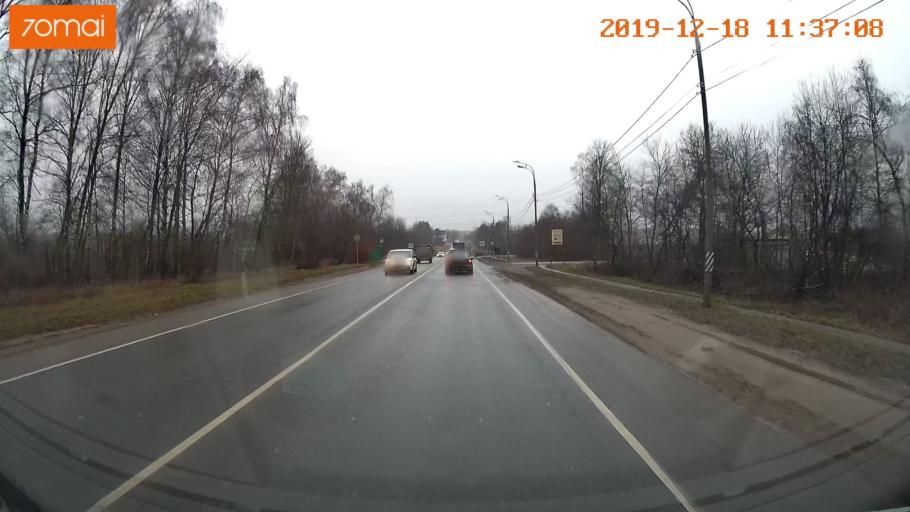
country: RU
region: Moskovskaya
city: Zvenigorod
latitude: 55.6879
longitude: 36.8981
